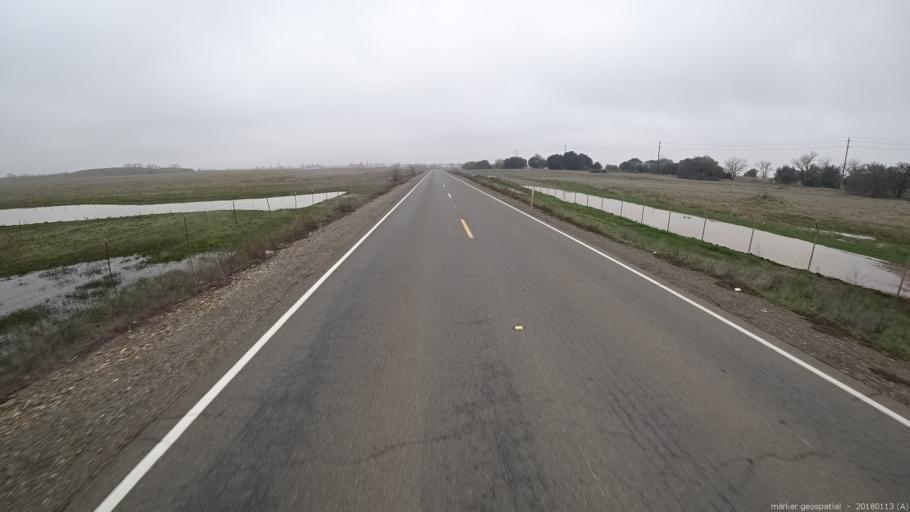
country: US
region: California
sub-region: Sacramento County
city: Gold River
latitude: 38.5922
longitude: -121.2393
